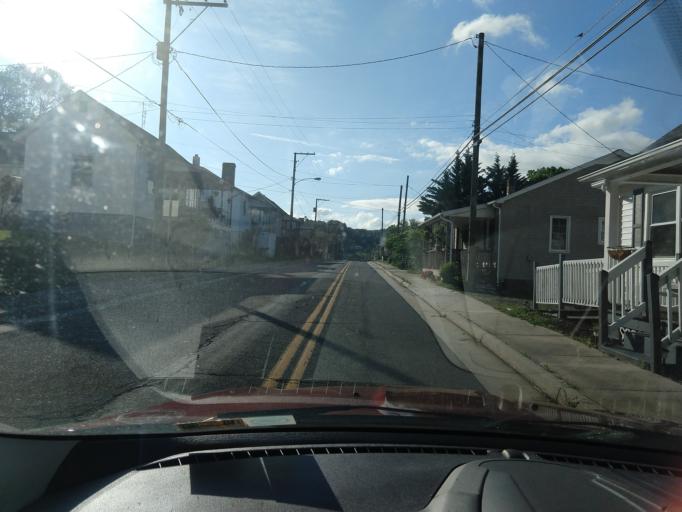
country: US
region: Virginia
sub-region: City of Galax
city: Galax
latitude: 36.7161
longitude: -80.9763
